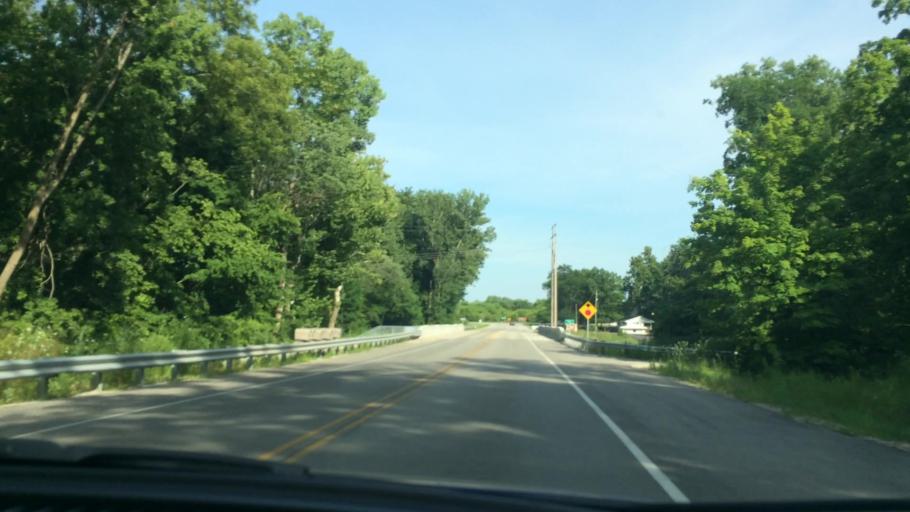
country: US
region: Indiana
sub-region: Tippecanoe County
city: Battle Ground
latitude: 40.4900
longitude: -86.8674
